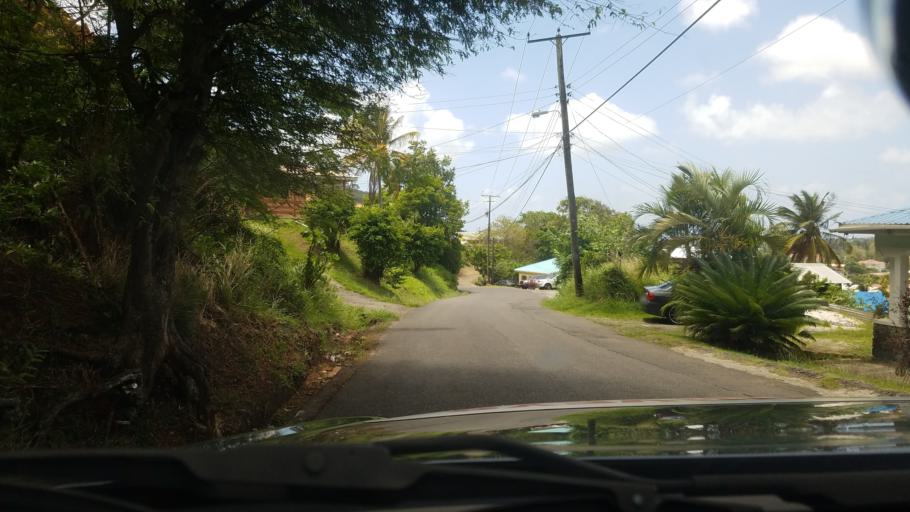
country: LC
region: Gros-Islet
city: Gros Islet
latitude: 14.0583
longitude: -60.9409
